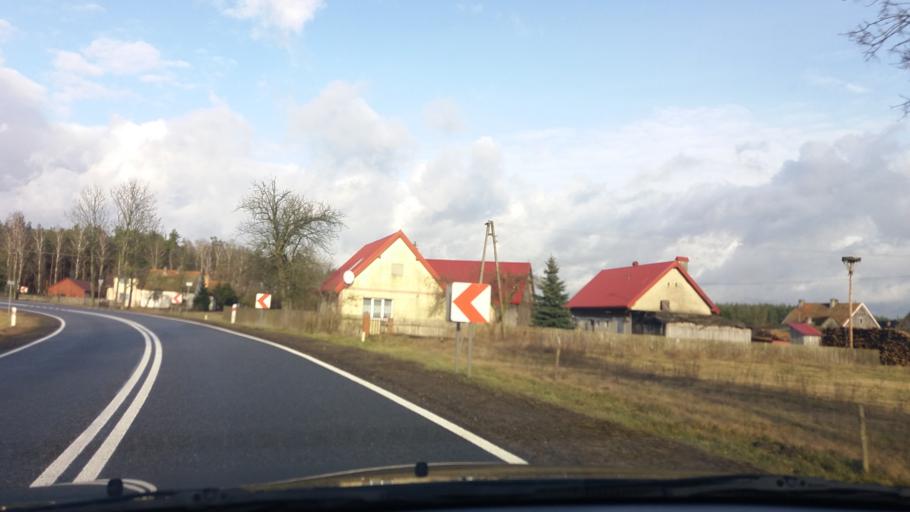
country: PL
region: Masovian Voivodeship
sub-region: Powiat przasnyski
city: Chorzele
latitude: 53.2921
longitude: 20.9159
